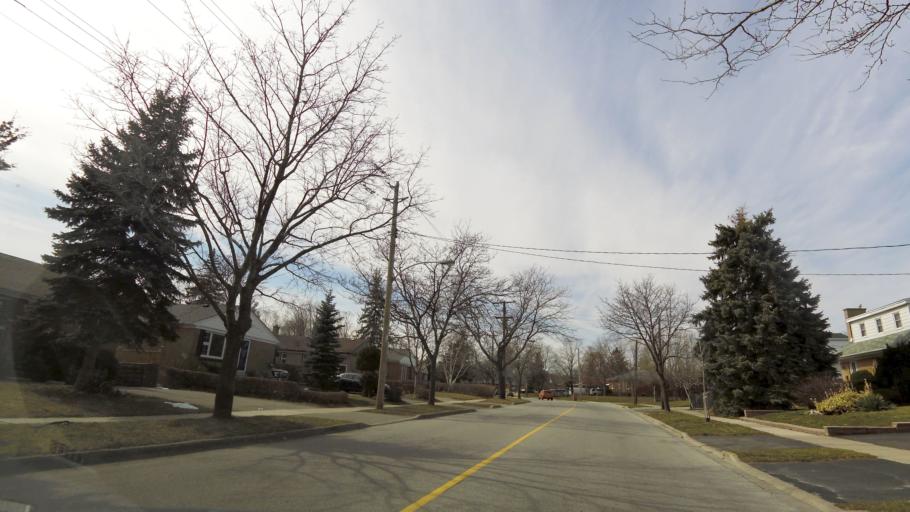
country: CA
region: Ontario
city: Burlington
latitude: 43.3577
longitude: -79.8232
